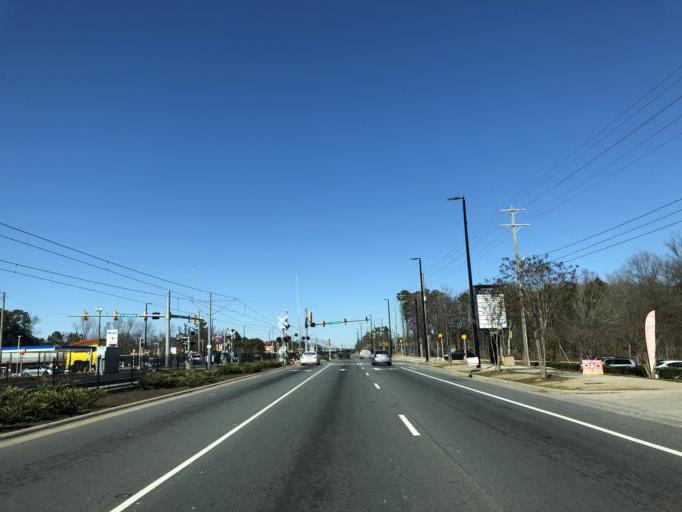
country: US
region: North Carolina
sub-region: Mecklenburg County
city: Charlotte
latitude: 35.2701
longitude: -80.7677
